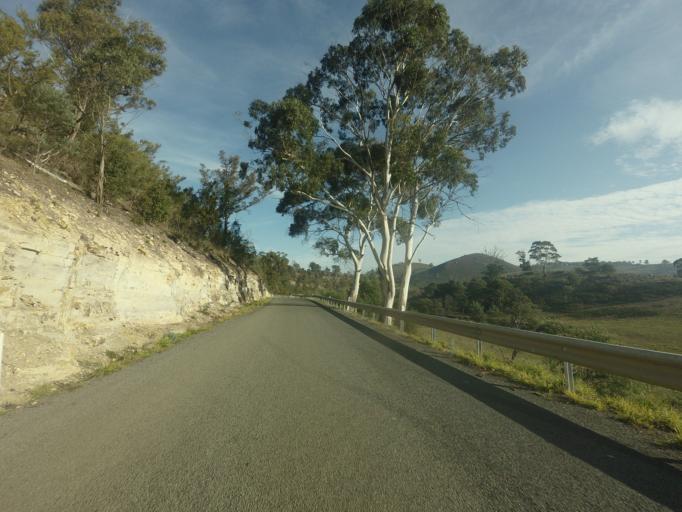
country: AU
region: Tasmania
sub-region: Brighton
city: Bridgewater
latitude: -42.5143
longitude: 147.4170
